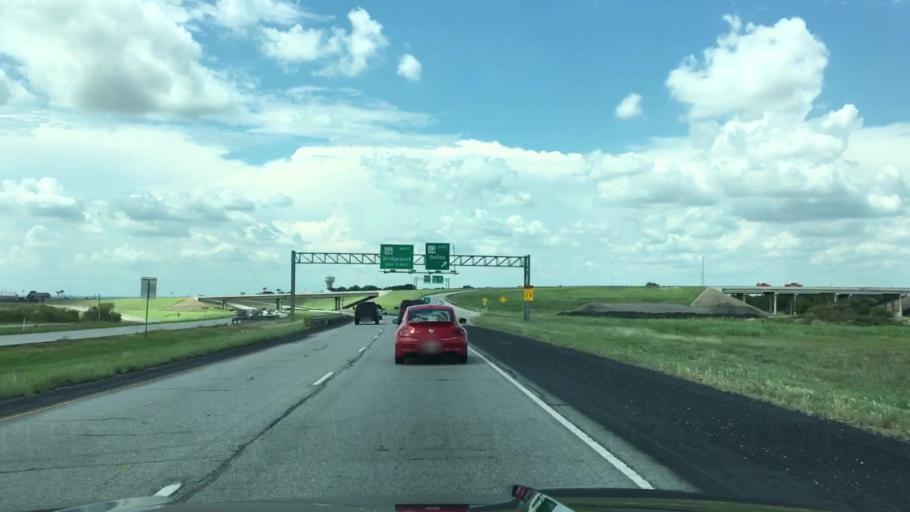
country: US
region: Texas
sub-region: Wise County
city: Rhome
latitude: 33.0430
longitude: -97.4598
